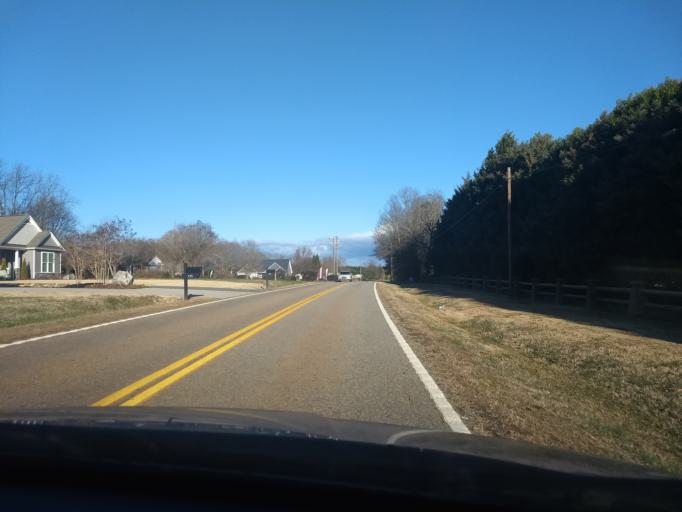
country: US
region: South Carolina
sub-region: Greenville County
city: Greer
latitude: 34.9839
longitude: -82.1997
